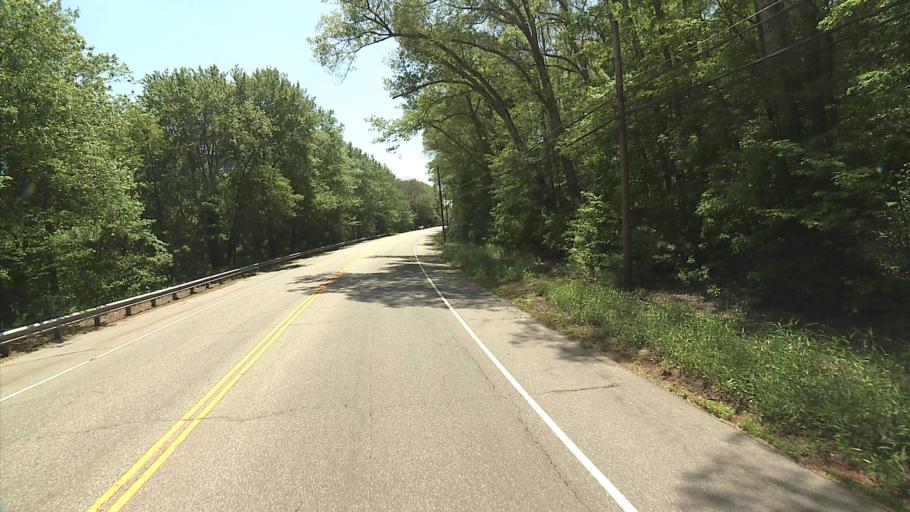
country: US
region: Connecticut
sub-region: Tolland County
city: Crystal Lake
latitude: 41.9021
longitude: -72.3924
